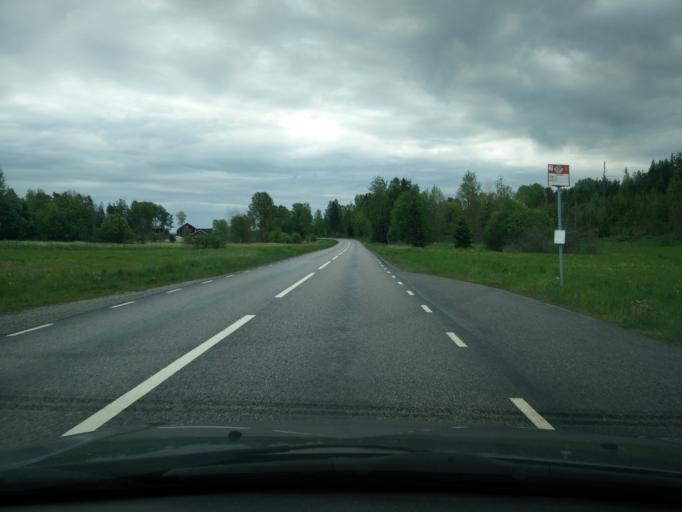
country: SE
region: Stockholm
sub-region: Norrtalje Kommun
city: Norrtalje
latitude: 59.7804
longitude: 18.8013
